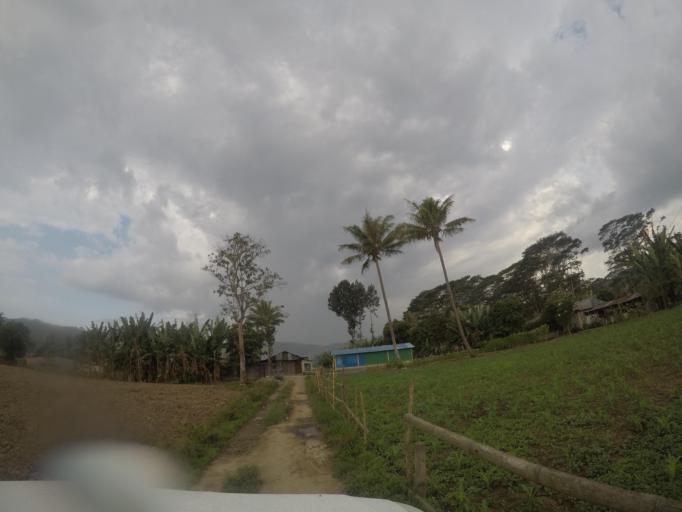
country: TL
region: Ermera
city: Gleno
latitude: -8.7229
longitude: 125.4395
